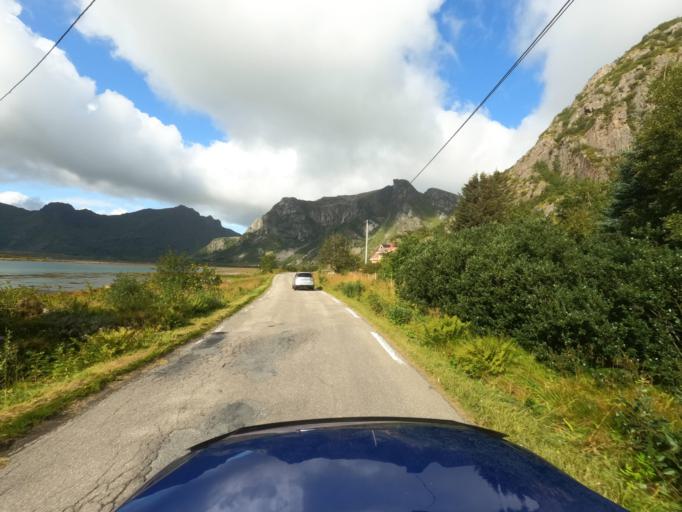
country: NO
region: Nordland
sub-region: Vestvagoy
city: Evjen
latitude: 68.1947
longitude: 14.0024
